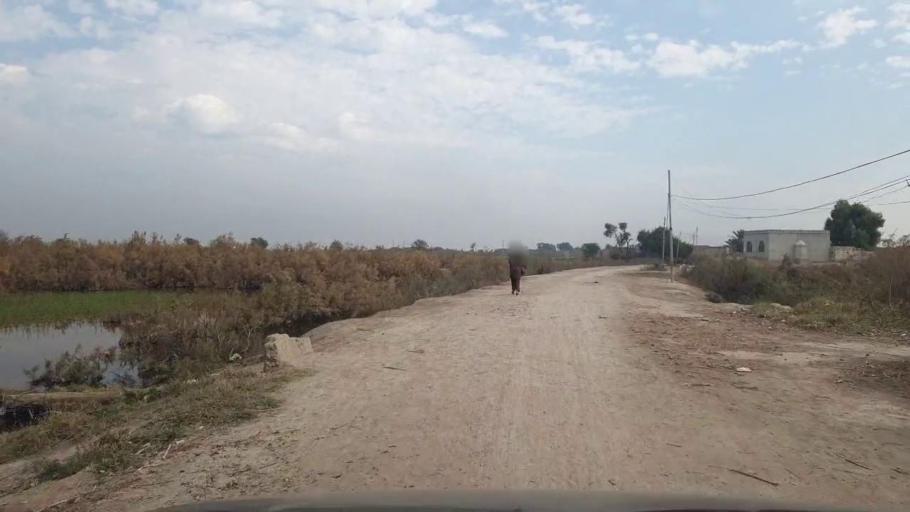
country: PK
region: Sindh
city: Sakrand
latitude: 26.0260
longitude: 68.4015
